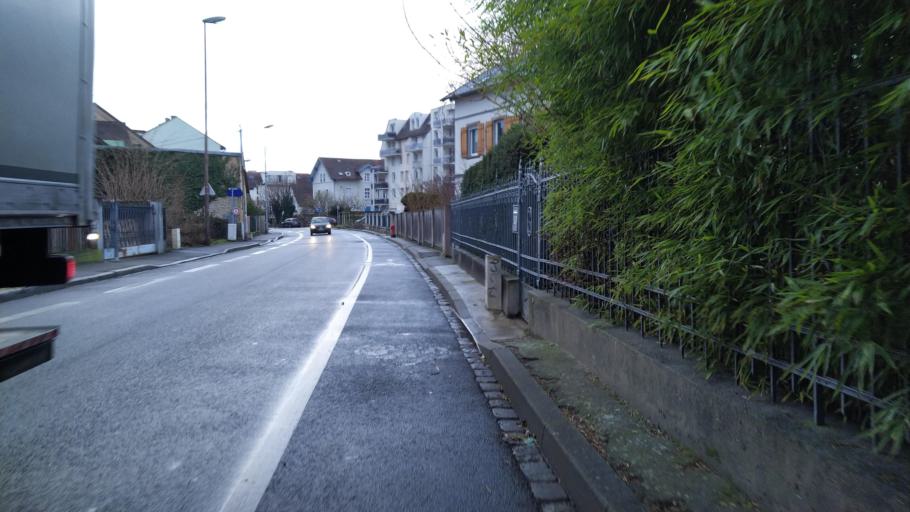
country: FR
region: Alsace
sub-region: Departement du Bas-Rhin
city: Schiltigheim
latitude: 48.6003
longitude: 7.7475
